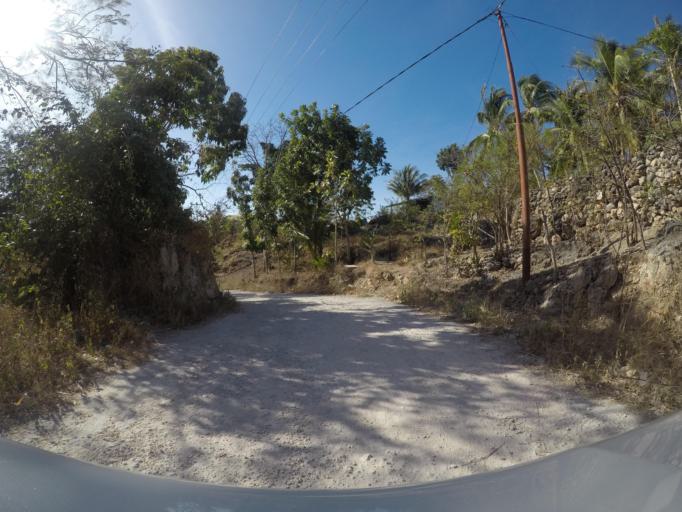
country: TL
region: Baucau
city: Baucau
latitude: -8.4511
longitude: 126.4331
